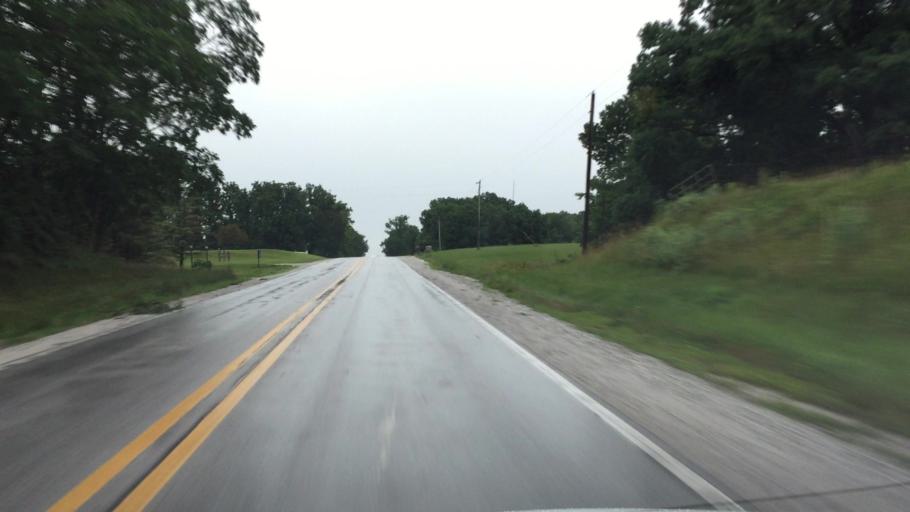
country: US
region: Illinois
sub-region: Hancock County
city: Carthage
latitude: 40.4368
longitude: -91.1400
